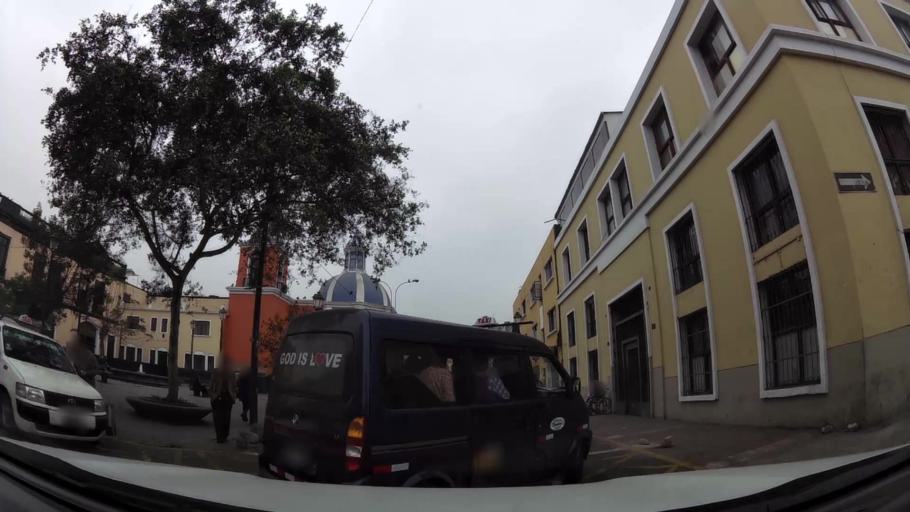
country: PE
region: Lima
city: Lima
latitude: -12.0474
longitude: -77.0227
